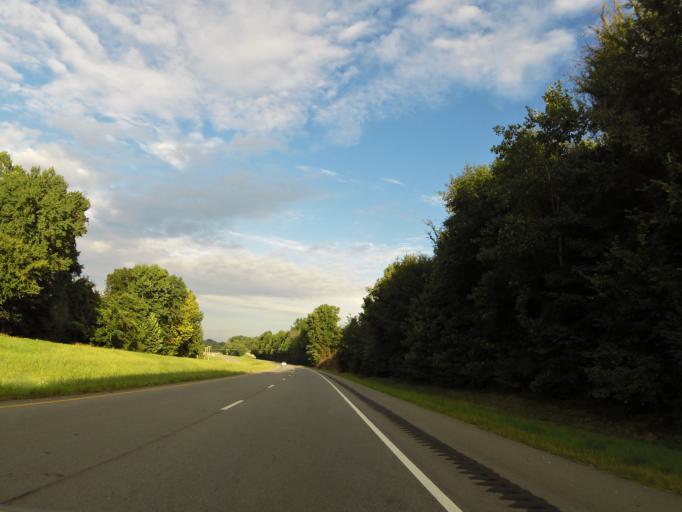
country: US
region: Alabama
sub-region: Lauderdale County
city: Rogersville
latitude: 34.8336
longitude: -87.3361
